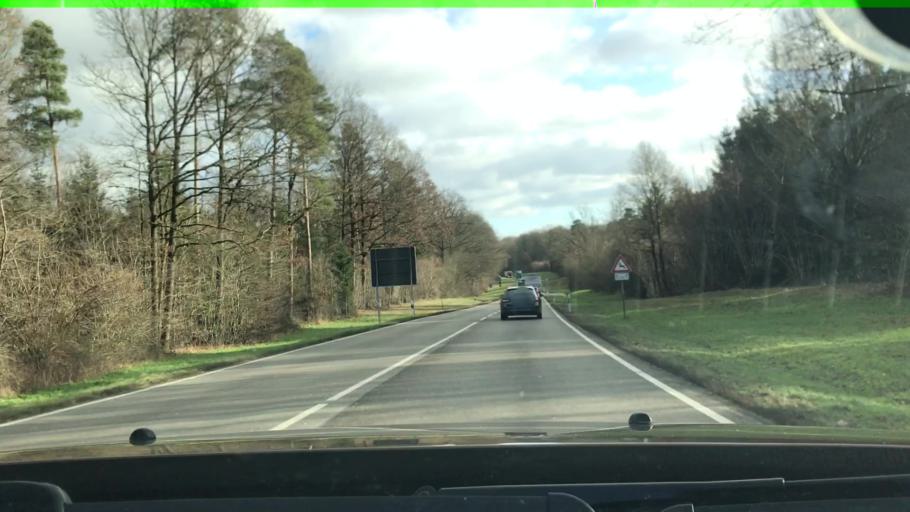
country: DE
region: Baden-Wuerttemberg
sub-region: Regierungsbezirk Stuttgart
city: Kirchberg an der Murr
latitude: 48.9841
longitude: 9.3485
